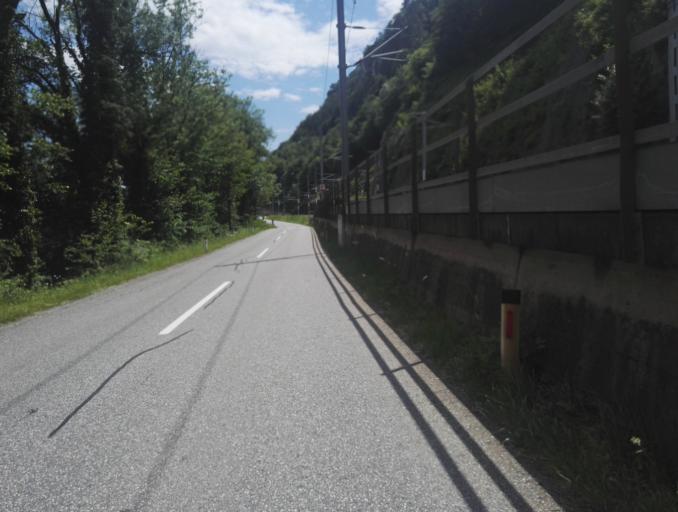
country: AT
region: Styria
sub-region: Politischer Bezirk Graz-Umgebung
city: Deutschfeistritz
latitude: 47.1553
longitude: 15.3177
